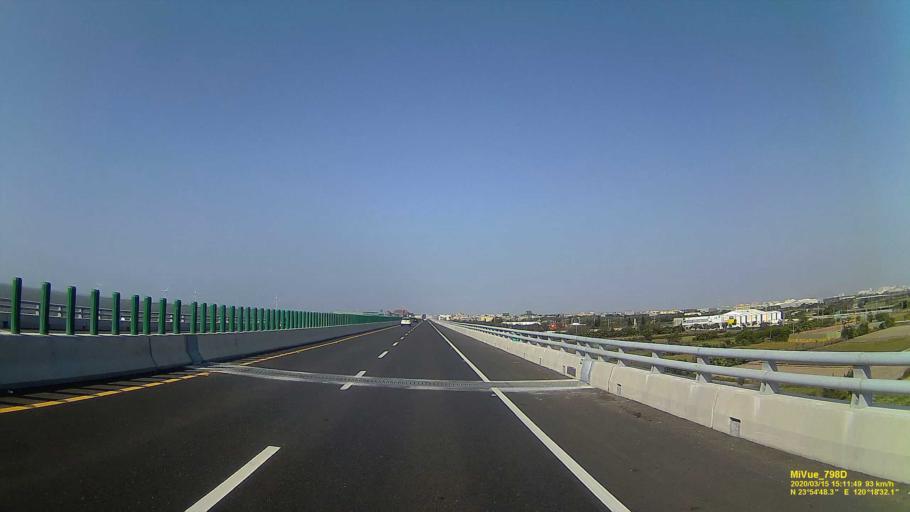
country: TW
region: Taiwan
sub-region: Changhua
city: Chang-hua
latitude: 23.9137
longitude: 120.3090
